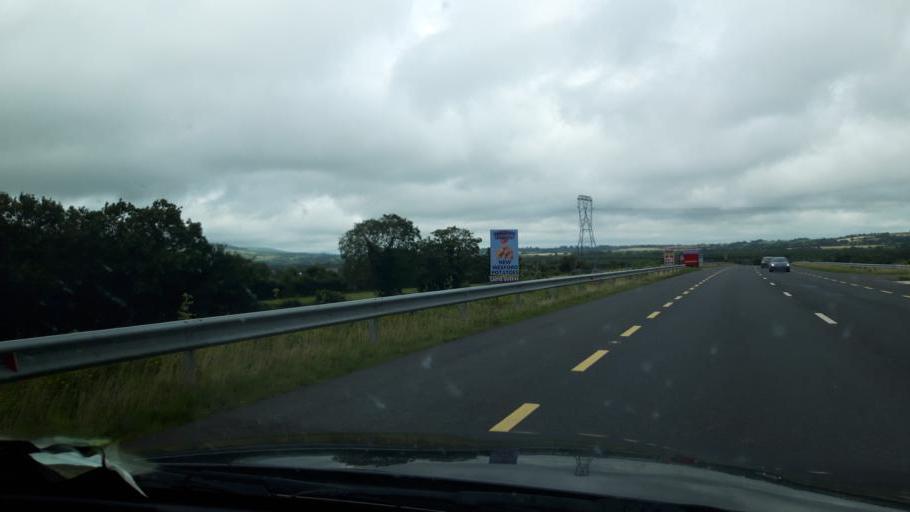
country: IE
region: Leinster
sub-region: Loch Garman
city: New Ross
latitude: 52.4202
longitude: -6.8569
